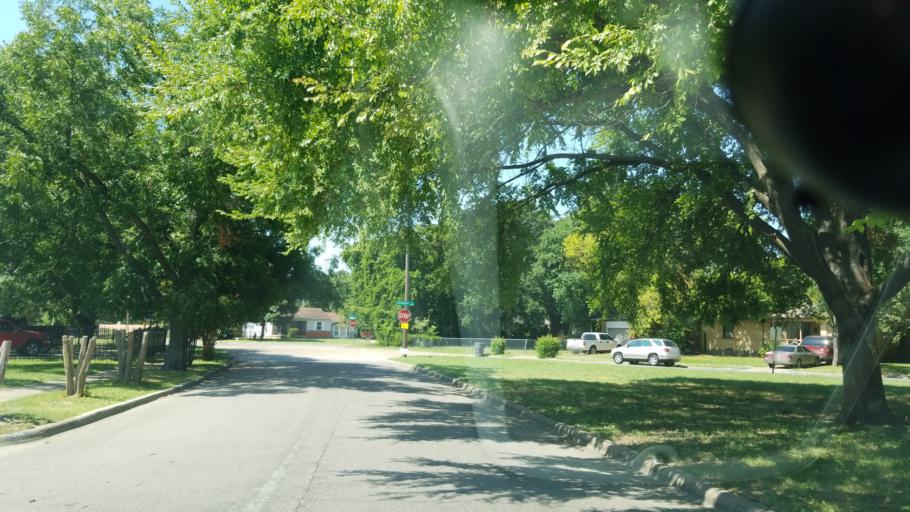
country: US
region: Texas
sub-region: Dallas County
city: Cockrell Hill
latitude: 32.7138
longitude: -96.8371
